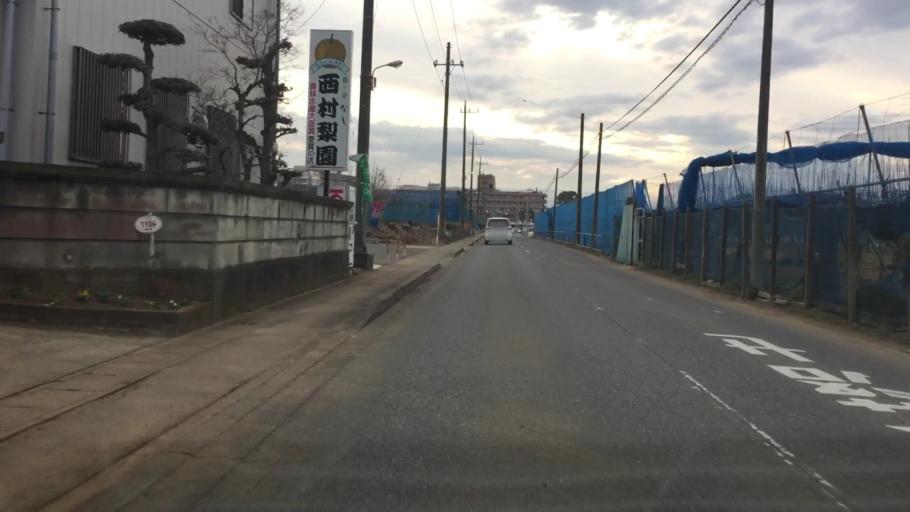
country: JP
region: Chiba
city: Kashiwa
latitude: 35.7883
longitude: 139.9900
